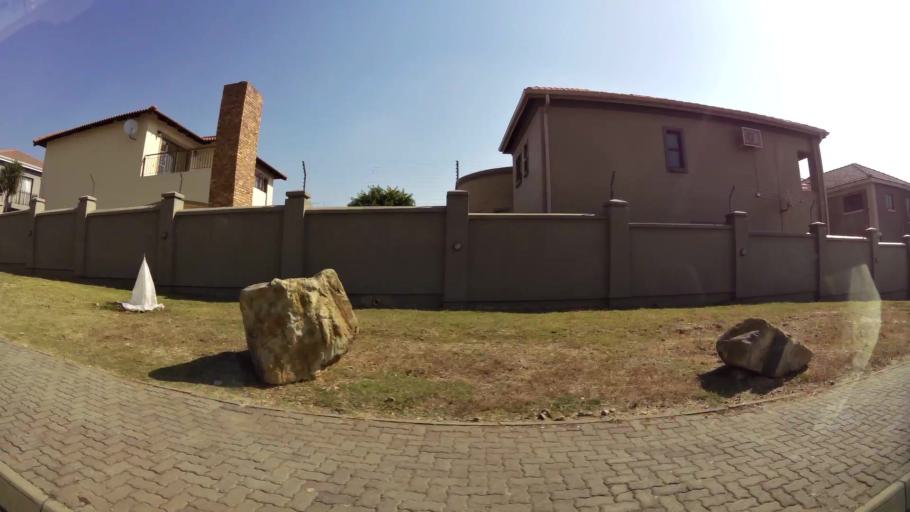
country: ZA
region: Gauteng
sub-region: City of Johannesburg Metropolitan Municipality
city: Modderfontein
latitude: -26.1148
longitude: 28.1633
